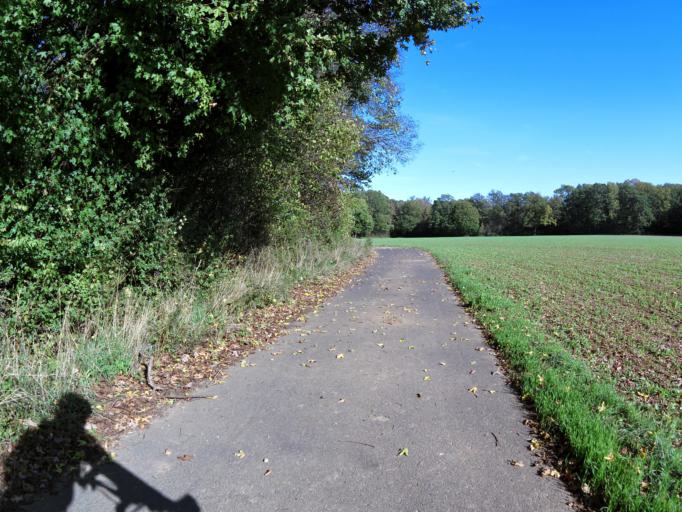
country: DE
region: Bavaria
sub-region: Regierungsbezirk Unterfranken
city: Sulzfeld am Main
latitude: 49.7158
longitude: 10.0944
